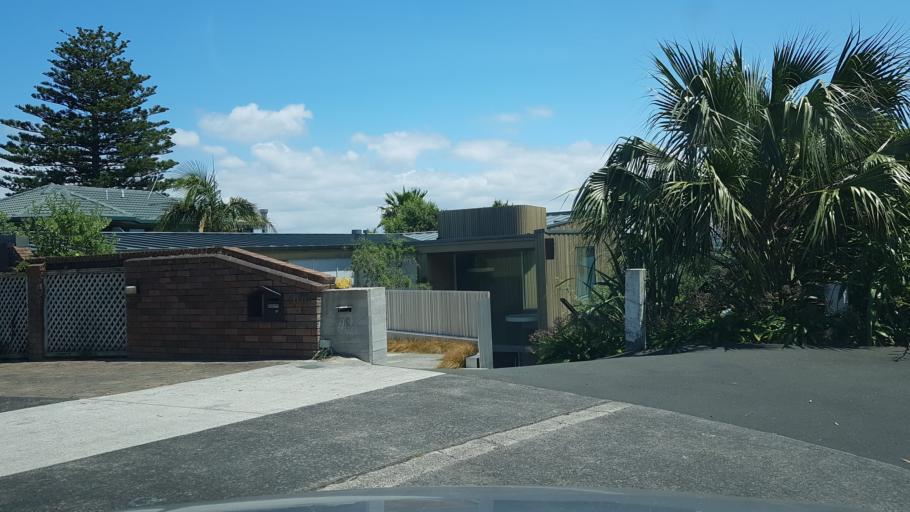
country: NZ
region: Auckland
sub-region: Auckland
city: North Shore
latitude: -36.8280
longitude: 174.7730
